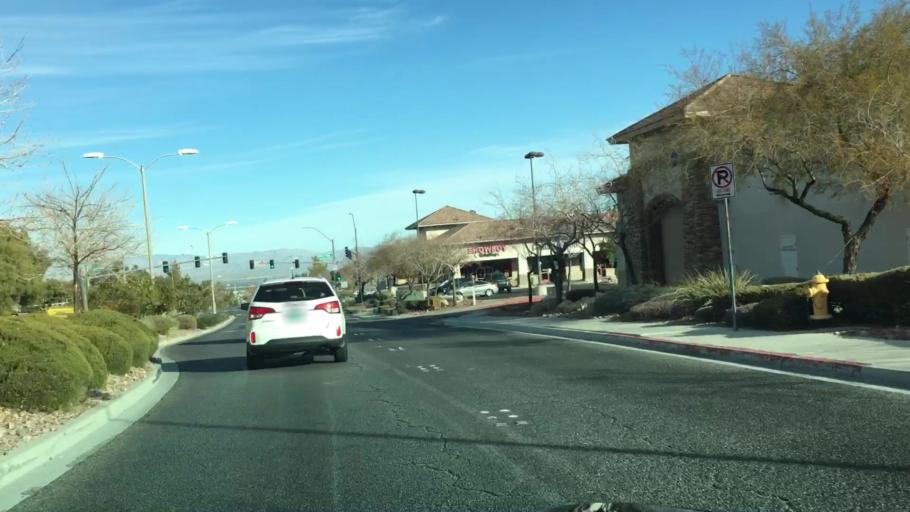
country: US
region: Nevada
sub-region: Clark County
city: Whitney
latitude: 35.9792
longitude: -115.1008
